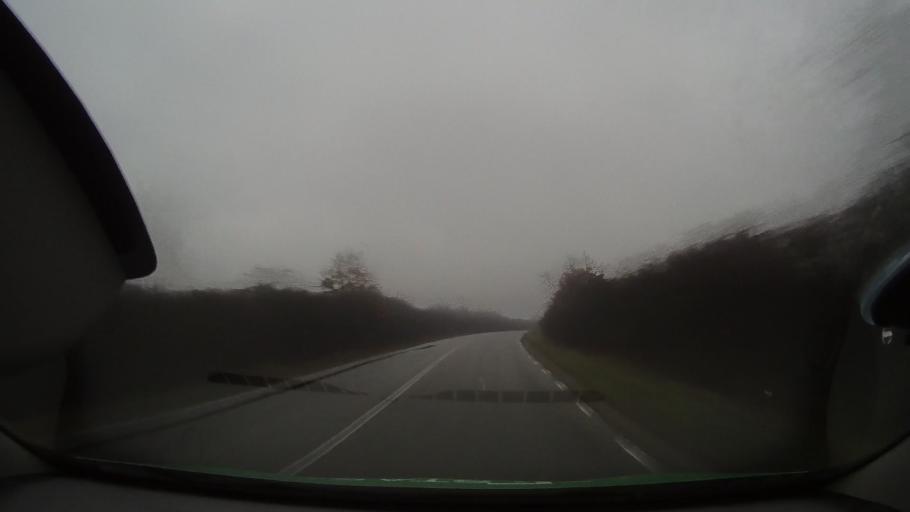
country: RO
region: Arad
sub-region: Comuna Craiova
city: Craiova
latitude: 46.6004
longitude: 21.9693
